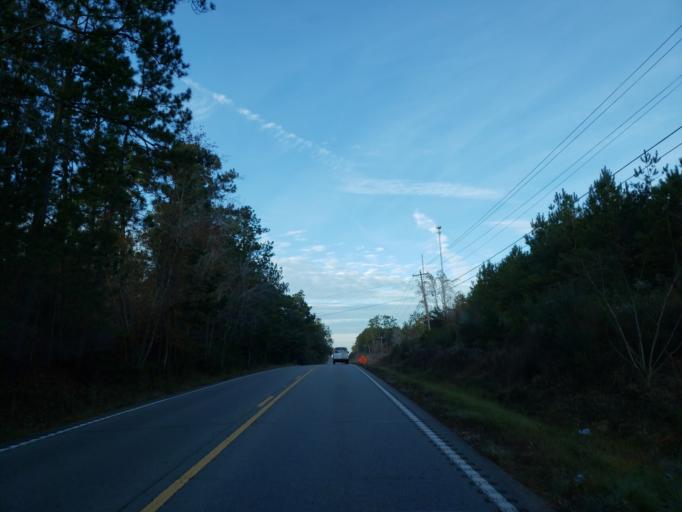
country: US
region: Mississippi
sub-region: Lamar County
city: West Hattiesburg
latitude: 31.2488
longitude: -89.3429
